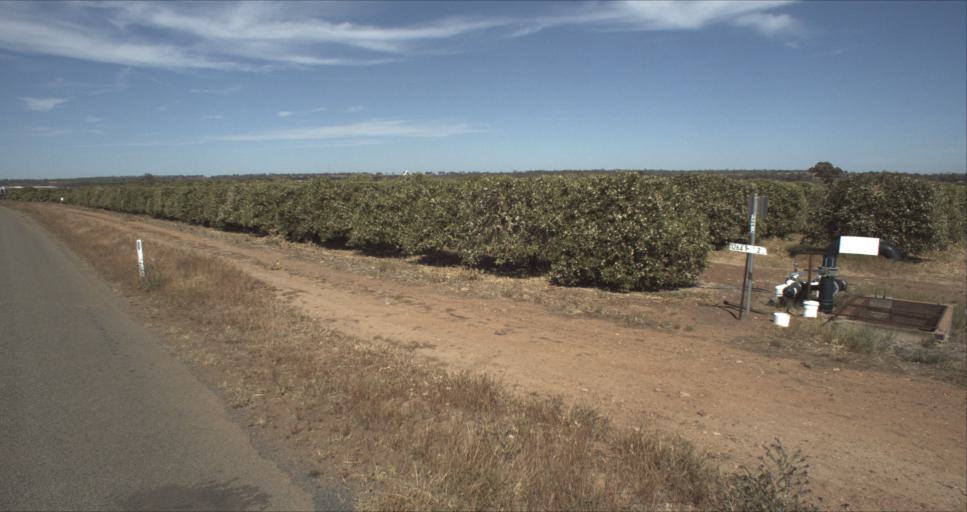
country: AU
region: New South Wales
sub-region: Leeton
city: Leeton
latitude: -34.5793
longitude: 146.4778
